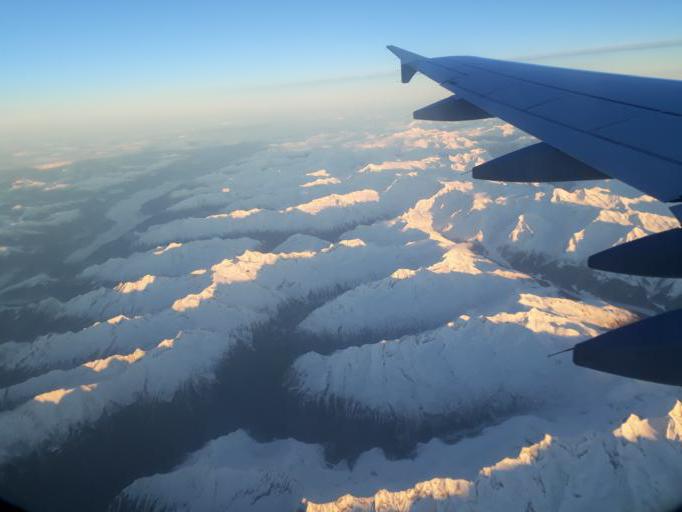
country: AT
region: Tyrol
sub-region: Politischer Bezirk Schwaz
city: Mayrhofen
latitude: 47.0872
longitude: 11.8714
